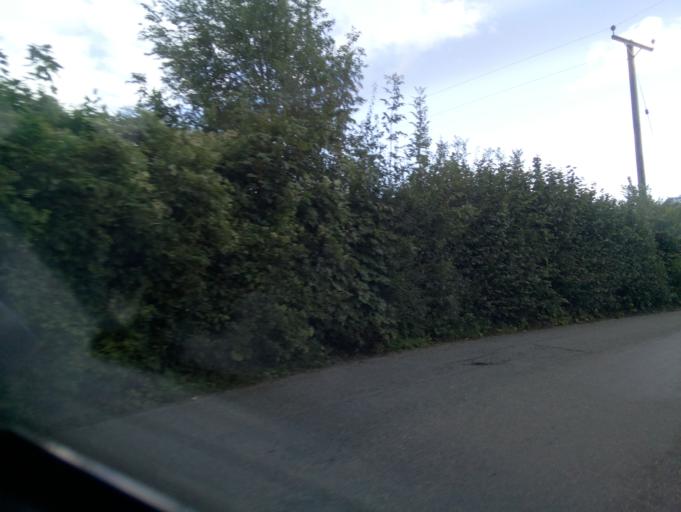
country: GB
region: England
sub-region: Devon
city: Ivybridge
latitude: 50.3729
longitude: -3.9129
